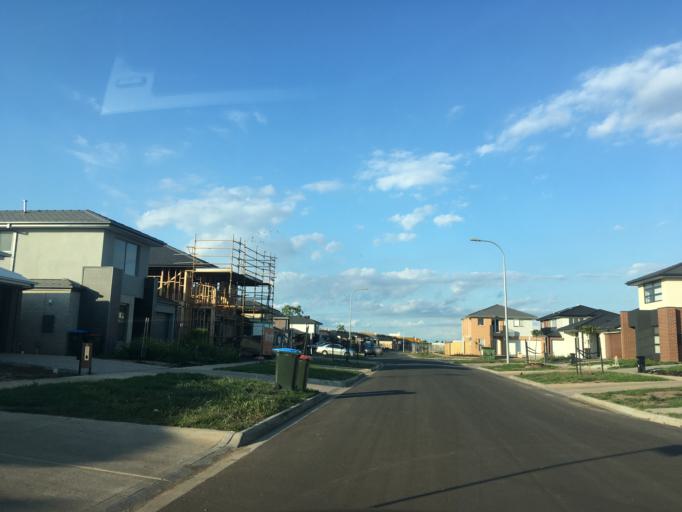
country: AU
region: Victoria
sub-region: Wyndham
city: Hoppers Crossing
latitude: -37.8801
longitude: 144.7163
